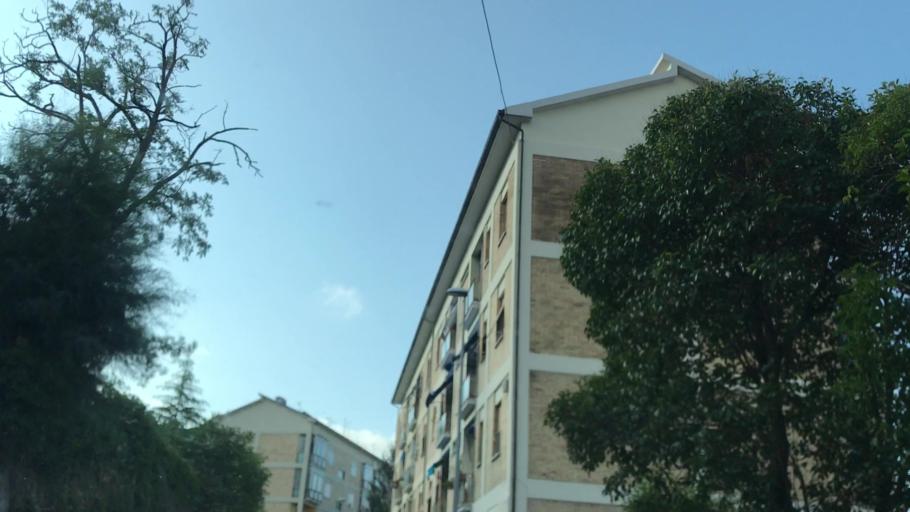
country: IT
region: The Marches
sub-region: Provincia di Ancona
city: Le Grazie di Ancona
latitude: 43.5947
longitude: 13.5168
